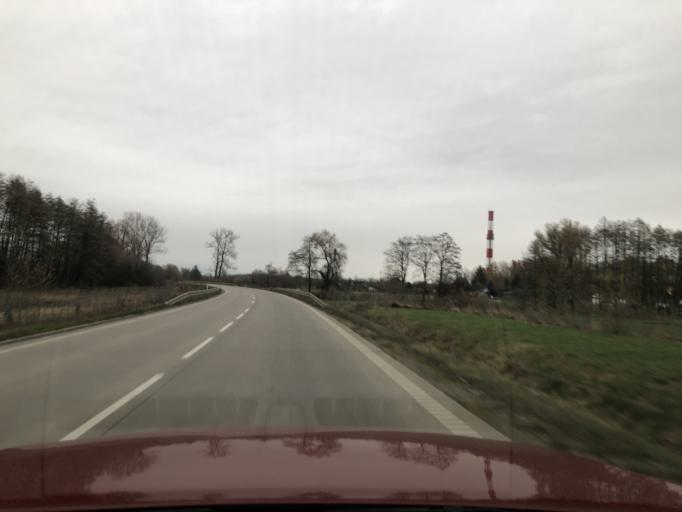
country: PL
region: Lower Silesian Voivodeship
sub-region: Powiat swidnicki
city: Swidnica
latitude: 50.8628
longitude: 16.4636
